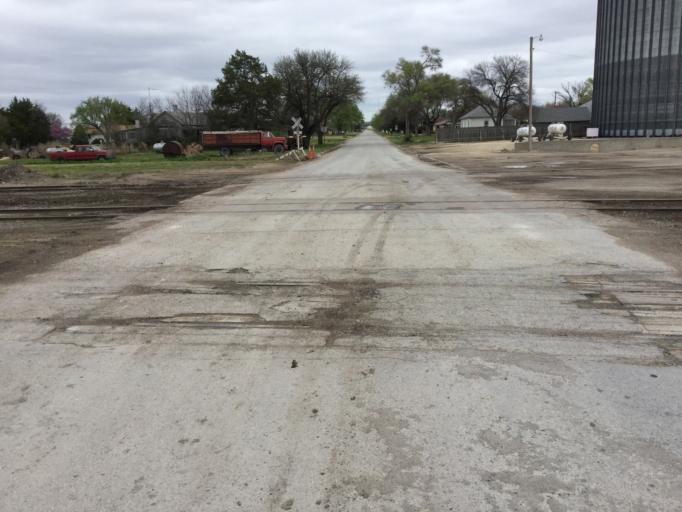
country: US
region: Kansas
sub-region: Osborne County
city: Osborne
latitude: 39.4433
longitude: -98.6966
